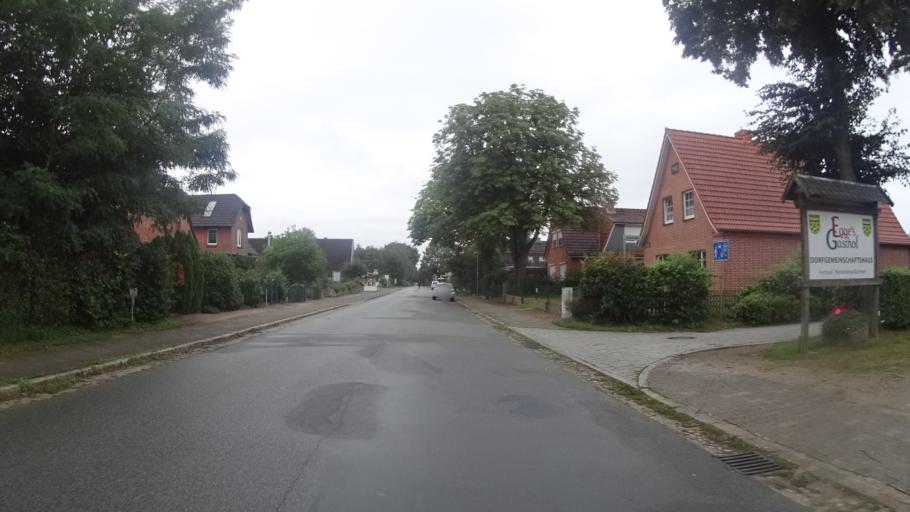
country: DE
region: Schleswig-Holstein
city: Guster
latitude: 53.5389
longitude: 10.6805
